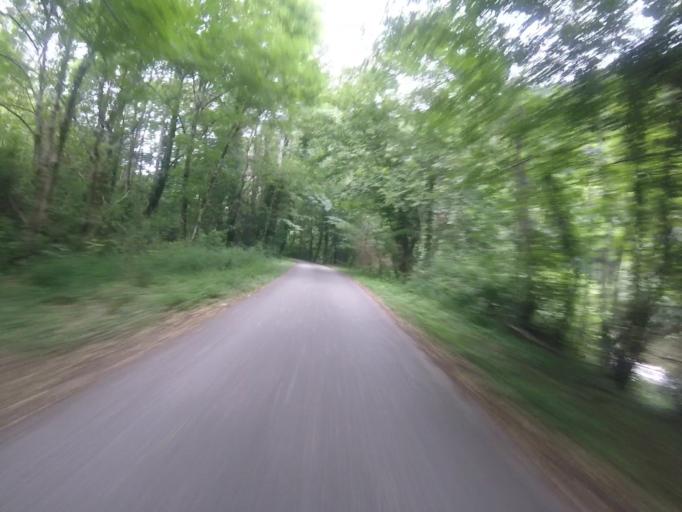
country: ES
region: Navarre
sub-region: Provincia de Navarra
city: Igantzi
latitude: 43.2171
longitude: -1.6712
